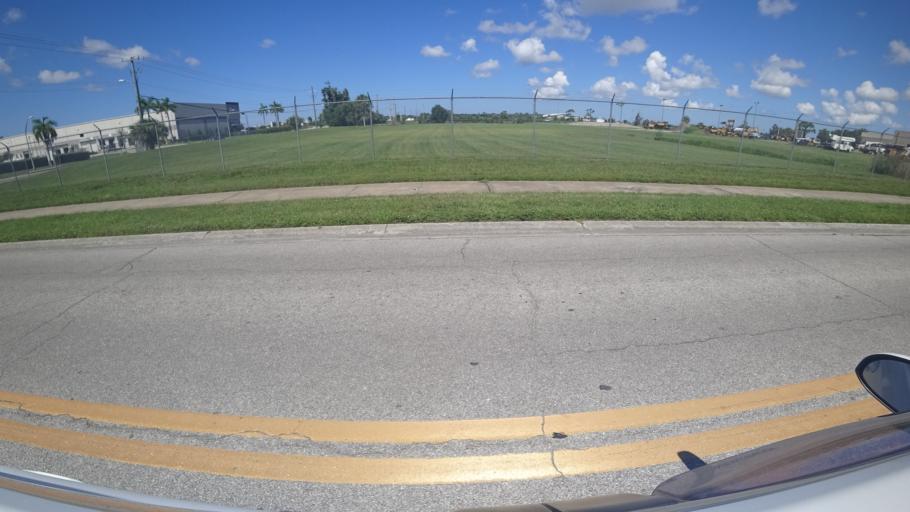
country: US
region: Florida
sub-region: Sarasota County
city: North Sarasota
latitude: 27.4040
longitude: -82.5308
